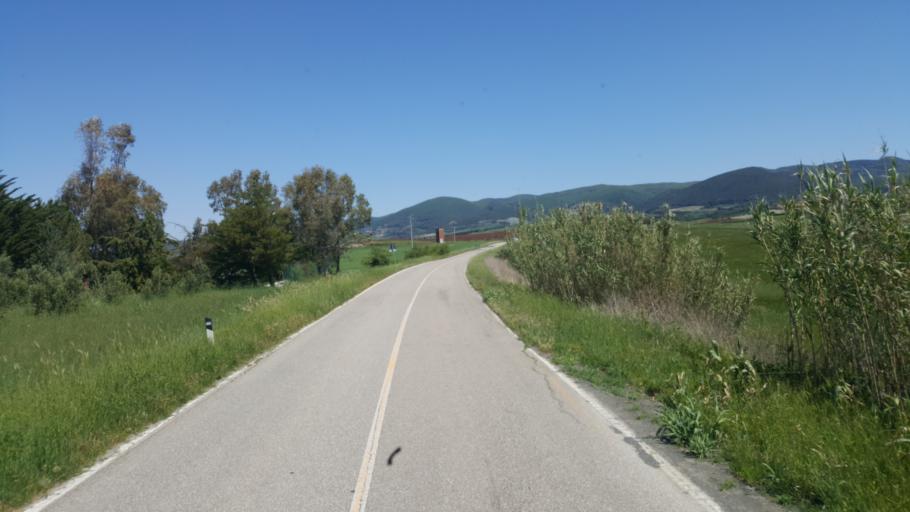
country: IT
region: Tuscany
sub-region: Province of Pisa
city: Castellina Marittima
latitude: 43.4223
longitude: 10.5265
